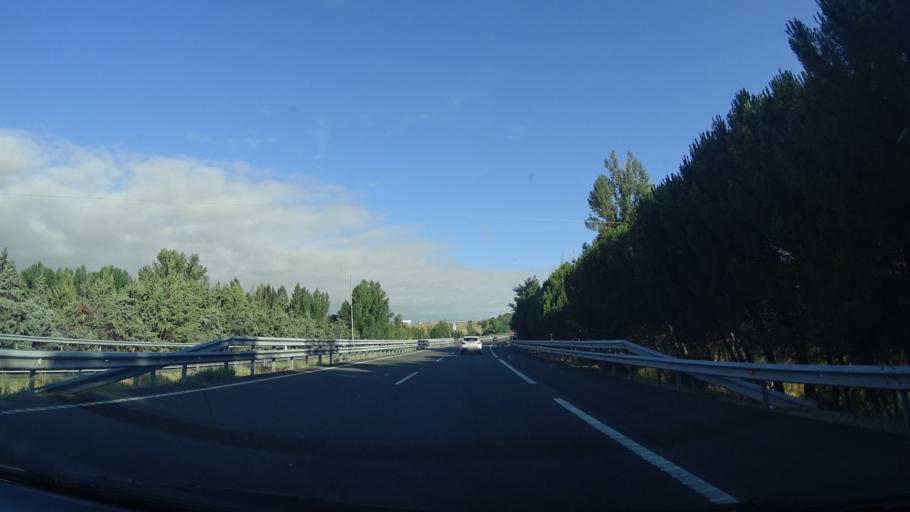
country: ES
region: Castille and Leon
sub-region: Provincia de Avila
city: Sanchidrian
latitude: 40.8639
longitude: -4.5625
